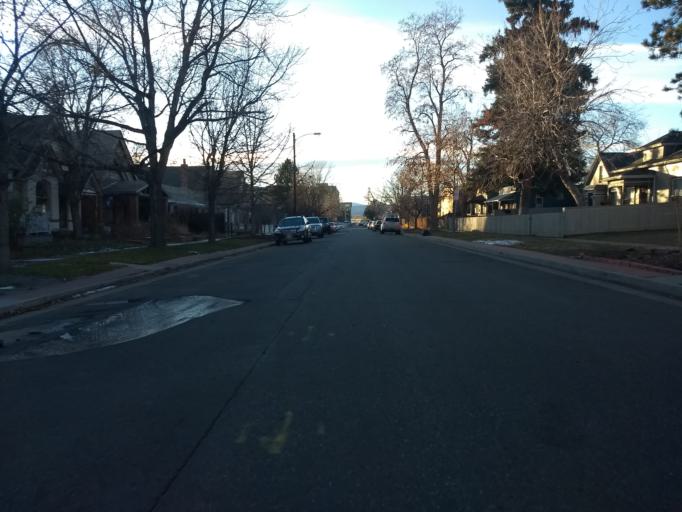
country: US
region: Colorado
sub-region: Denver County
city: Denver
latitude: 39.7130
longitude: -104.9907
